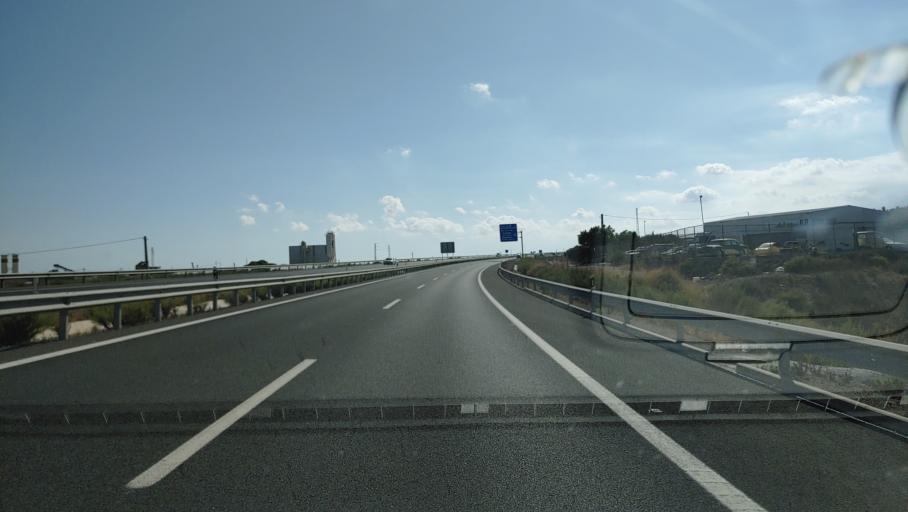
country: ES
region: Andalusia
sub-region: Provincia de Almeria
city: Roquetas de Mar
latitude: 36.7929
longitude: -2.6100
